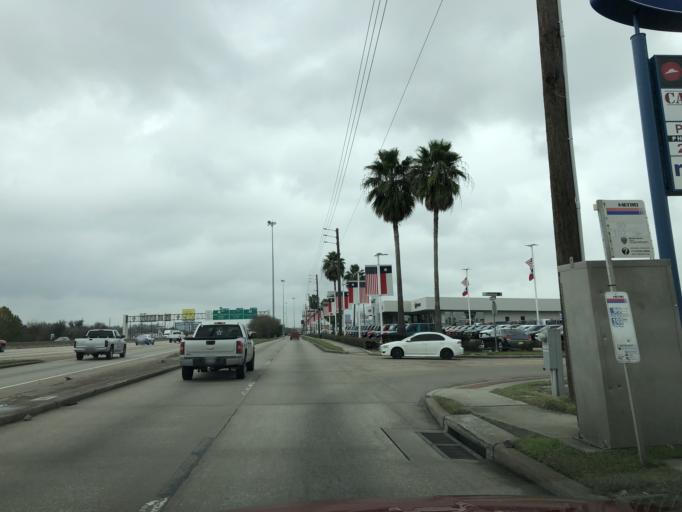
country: US
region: Texas
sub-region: Harris County
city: Aldine
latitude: 29.9242
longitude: -95.4118
